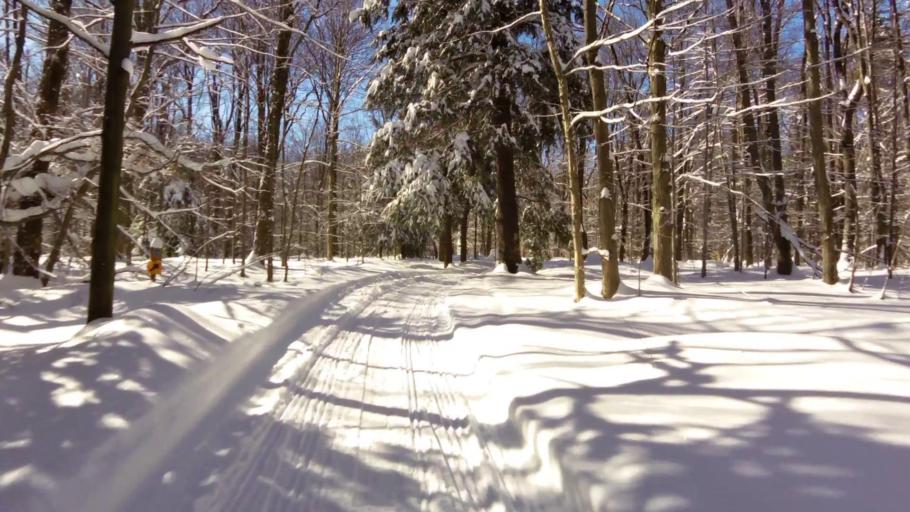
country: US
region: New York
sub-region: Chautauqua County
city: Fredonia
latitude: 42.3484
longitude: -79.1870
